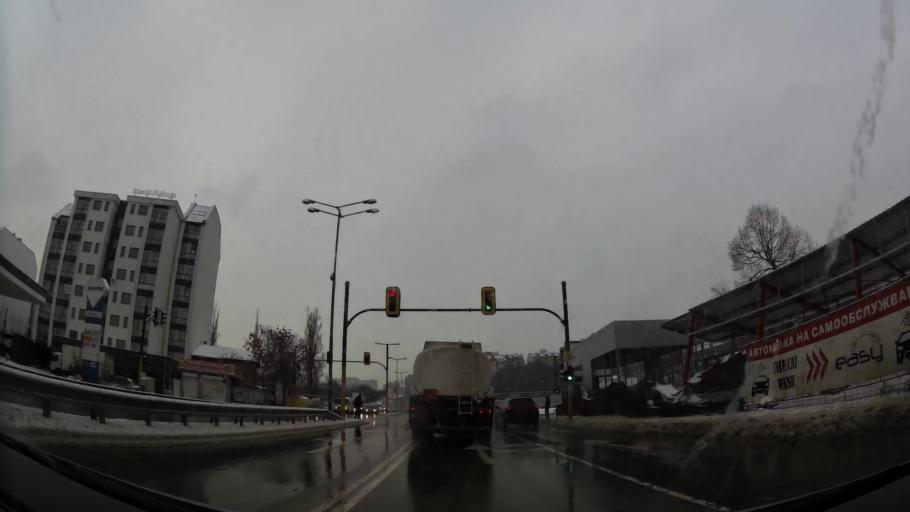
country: BG
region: Sofia-Capital
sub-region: Stolichna Obshtina
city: Sofia
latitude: 42.6924
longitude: 23.2950
